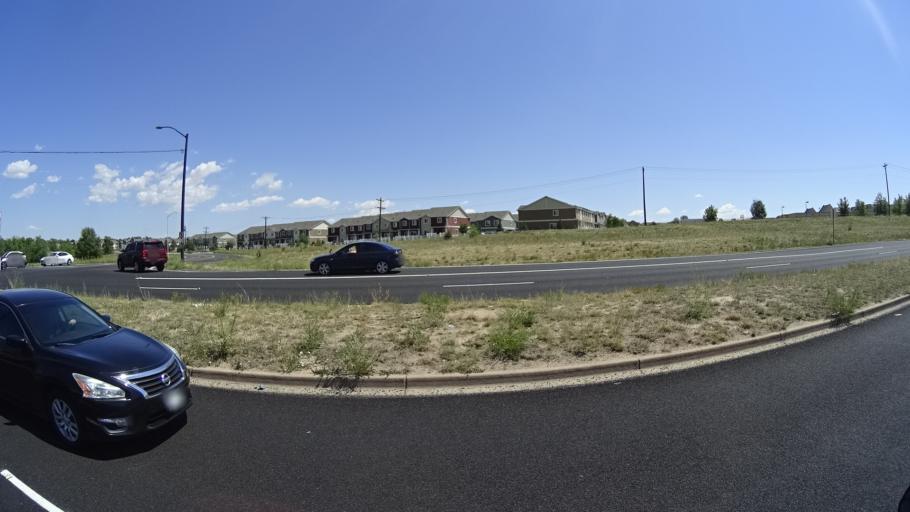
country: US
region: Colorado
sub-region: El Paso County
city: Stratmoor
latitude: 38.7862
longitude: -104.7399
